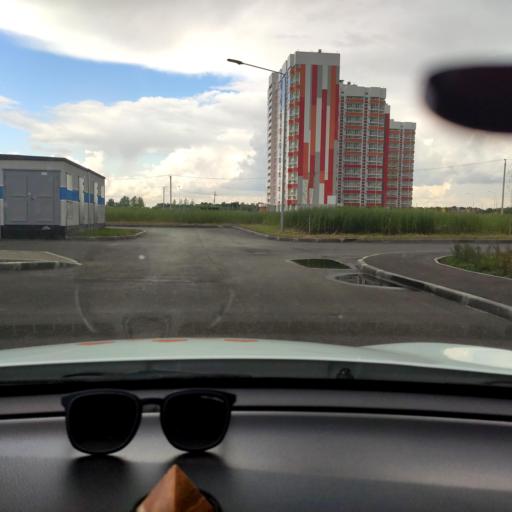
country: RU
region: Tatarstan
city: Osinovo
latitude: 55.8576
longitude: 48.8961
